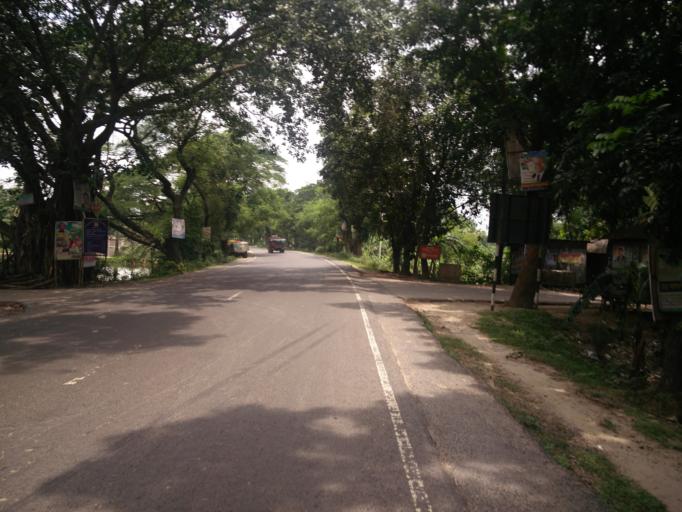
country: BD
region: Khulna
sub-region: Magura
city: Magura
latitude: 23.5438
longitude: 89.5333
